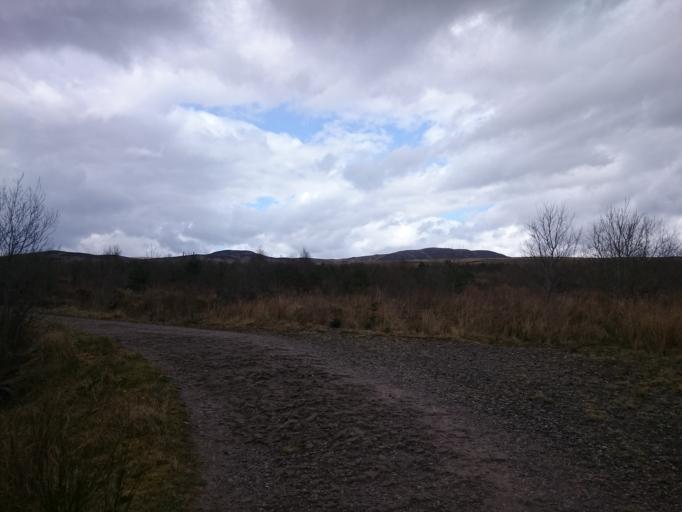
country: GB
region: Scotland
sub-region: Stirling
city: Killearn
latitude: 56.0916
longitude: -4.4844
